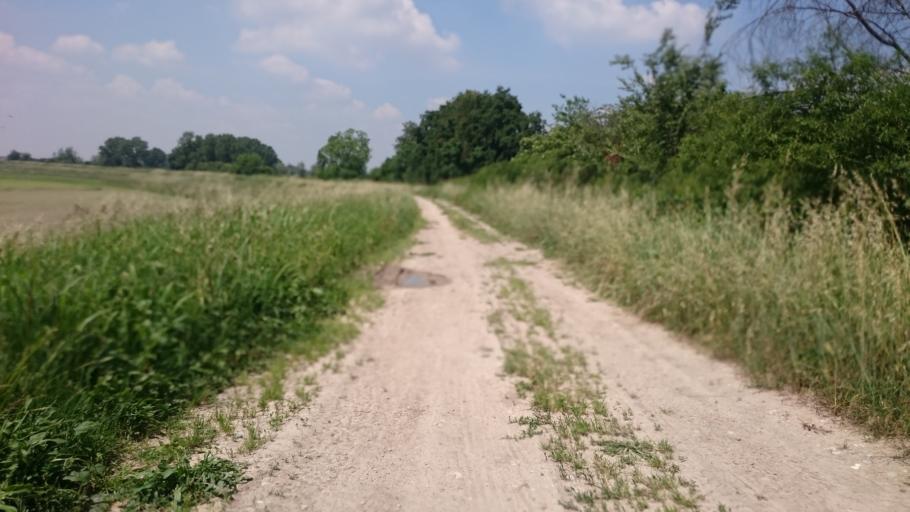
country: IT
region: Lombardy
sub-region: Provincia di Mantova
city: San Biagio
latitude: 45.1262
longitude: 10.8414
